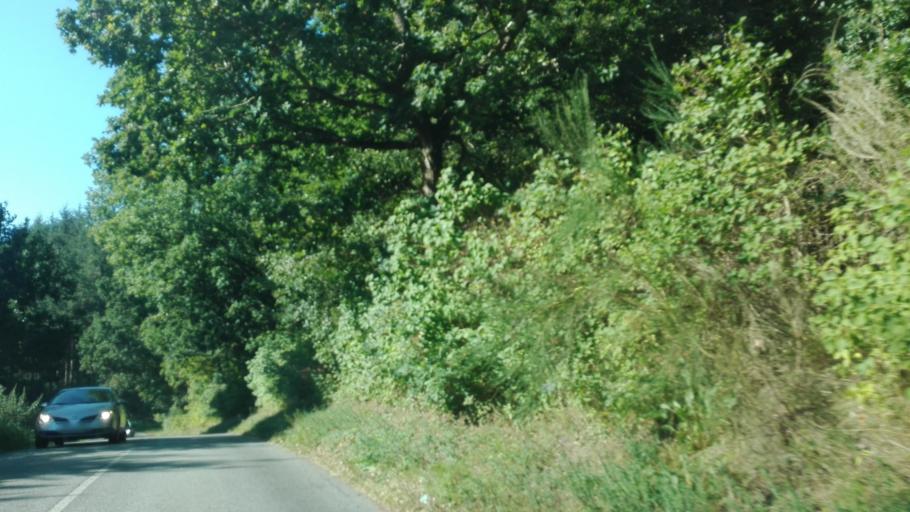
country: DK
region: Central Jutland
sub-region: Syddjurs Kommune
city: Ebeltoft
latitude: 56.2581
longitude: 10.6239
